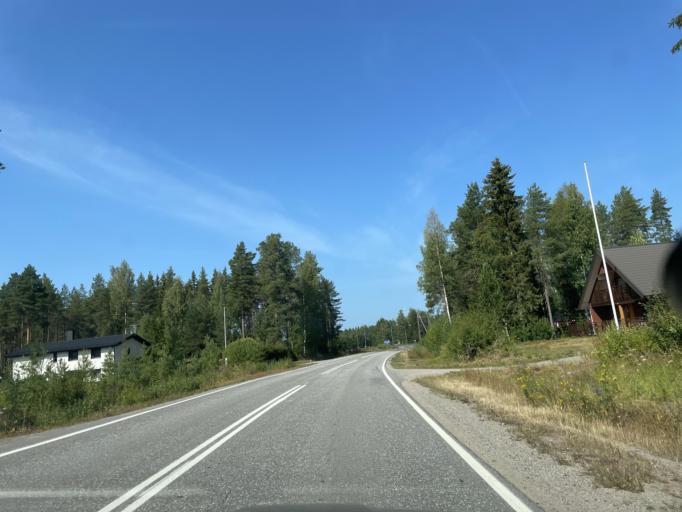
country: FI
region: Central Finland
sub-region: Saarijaervi-Viitasaari
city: Pihtipudas
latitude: 63.3755
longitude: 25.5949
